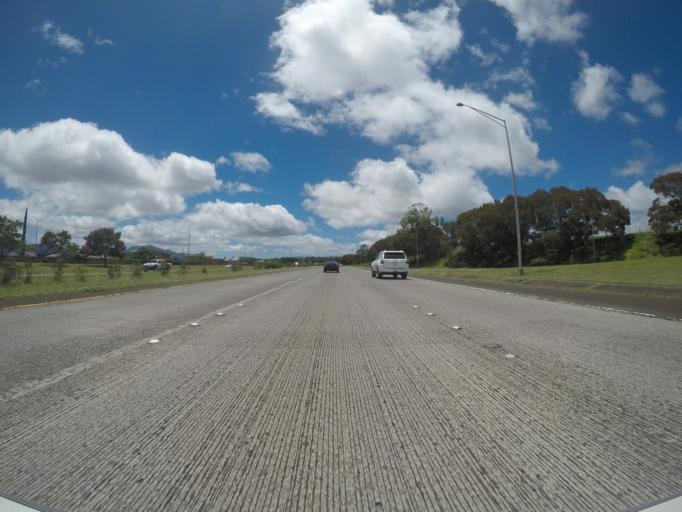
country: US
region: Hawaii
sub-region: Honolulu County
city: Waipi'o Acres
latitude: 21.4674
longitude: -158.0057
